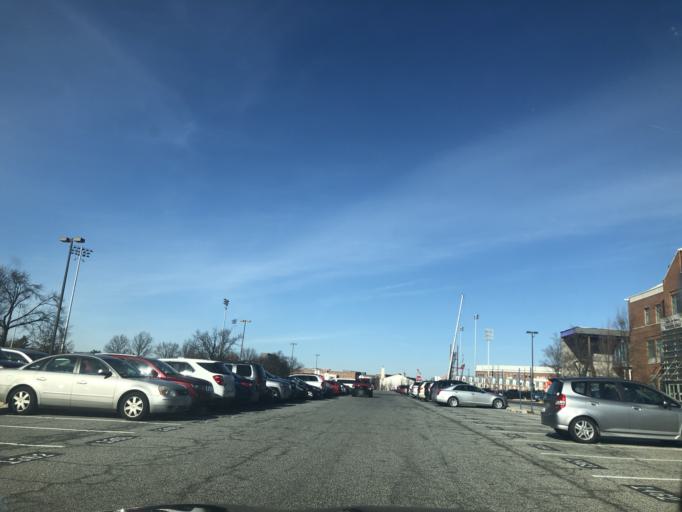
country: US
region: Maryland
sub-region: Prince George's County
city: College Park
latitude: 38.9863
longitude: -76.9493
